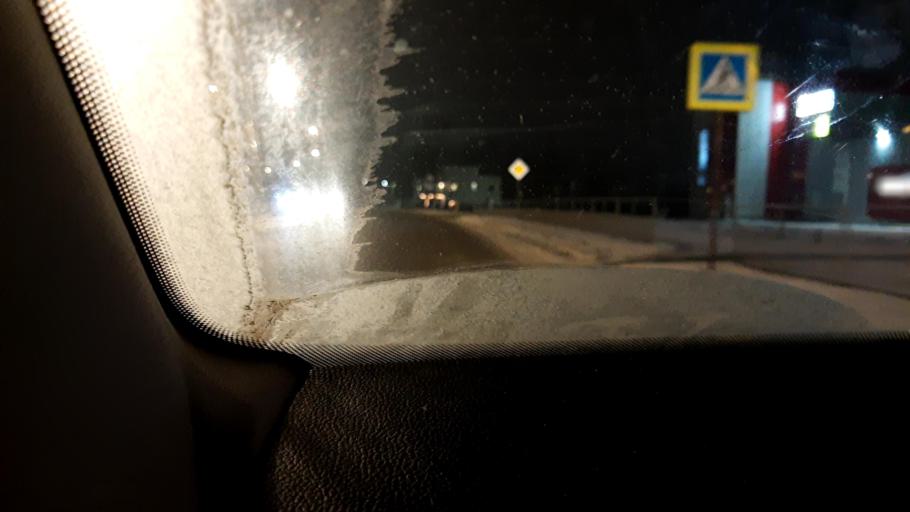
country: RU
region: Moskovskaya
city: Elektrostal'
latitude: 55.7642
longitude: 38.4457
